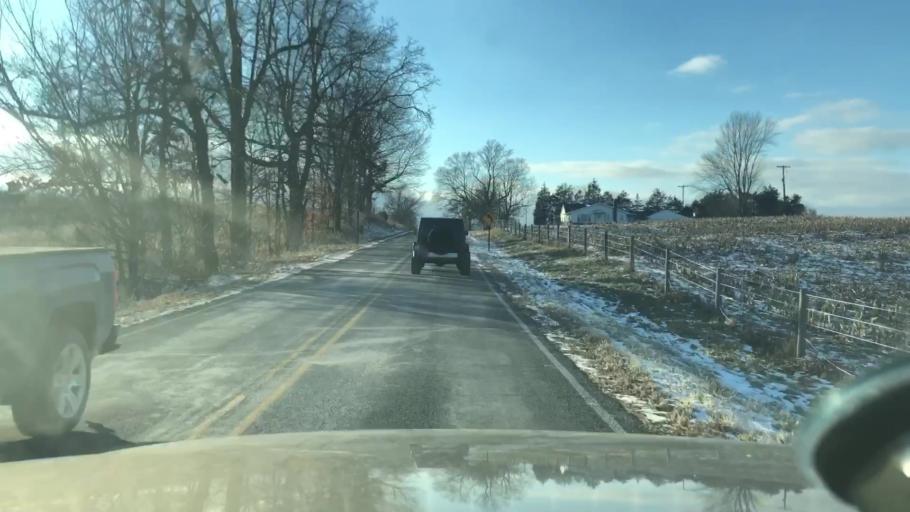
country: US
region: Michigan
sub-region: Jackson County
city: Vandercook Lake
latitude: 42.0974
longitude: -84.4525
